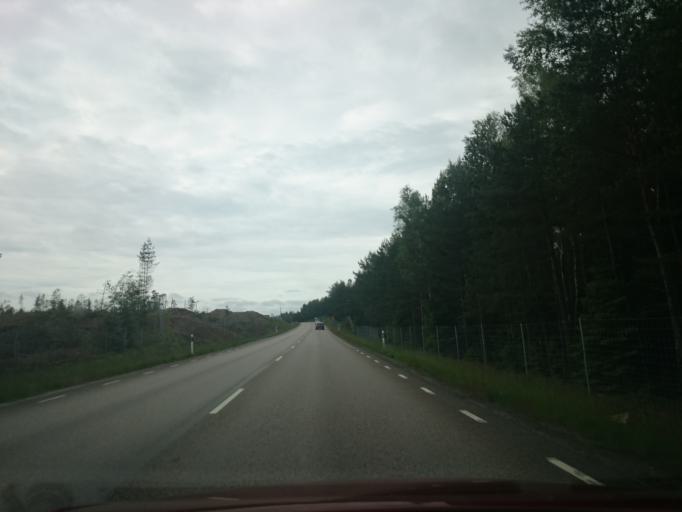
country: SE
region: Vaestra Goetaland
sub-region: Harryda Kommun
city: Hindas
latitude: 57.6830
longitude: 12.3634
